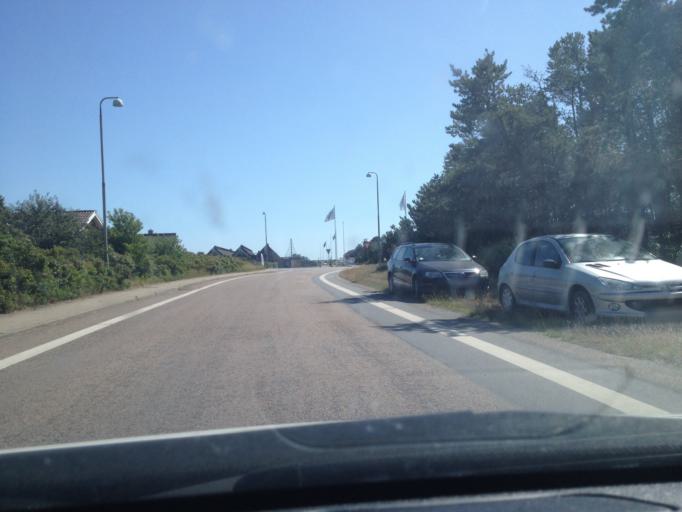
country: DE
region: Schleswig-Holstein
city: List
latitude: 55.0885
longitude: 8.5514
